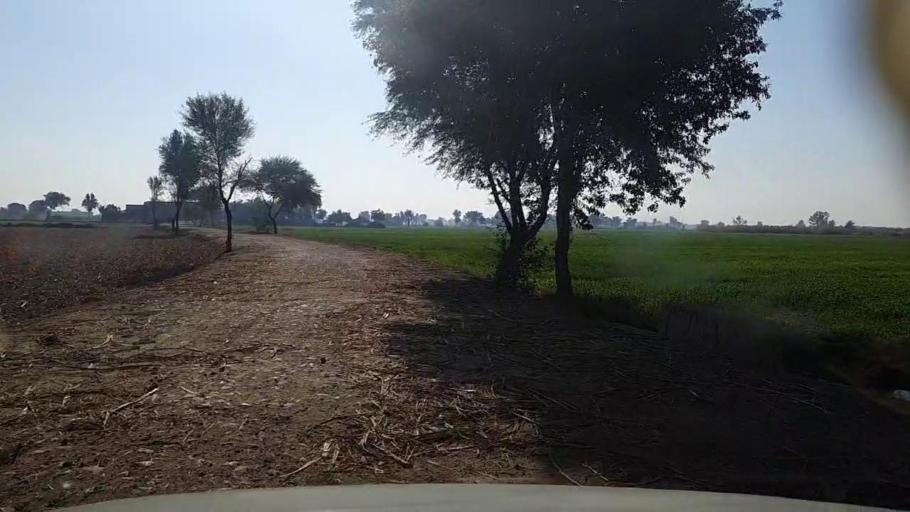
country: PK
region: Sindh
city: Khairpur
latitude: 28.0561
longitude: 69.7375
